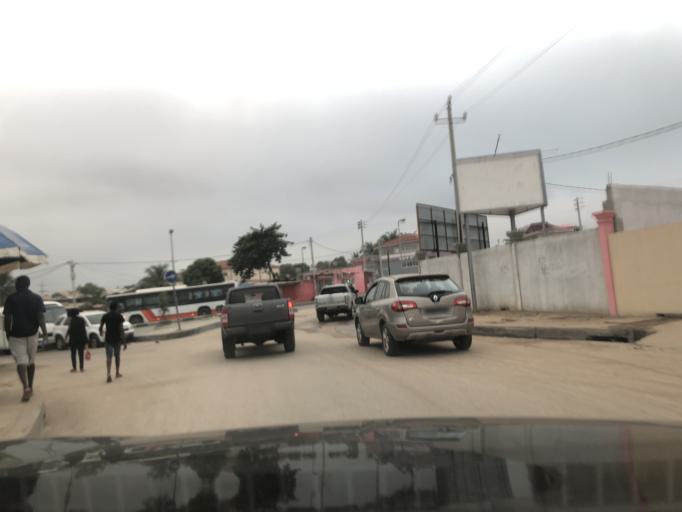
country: AO
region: Luanda
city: Luanda
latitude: -8.8480
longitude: 13.2124
